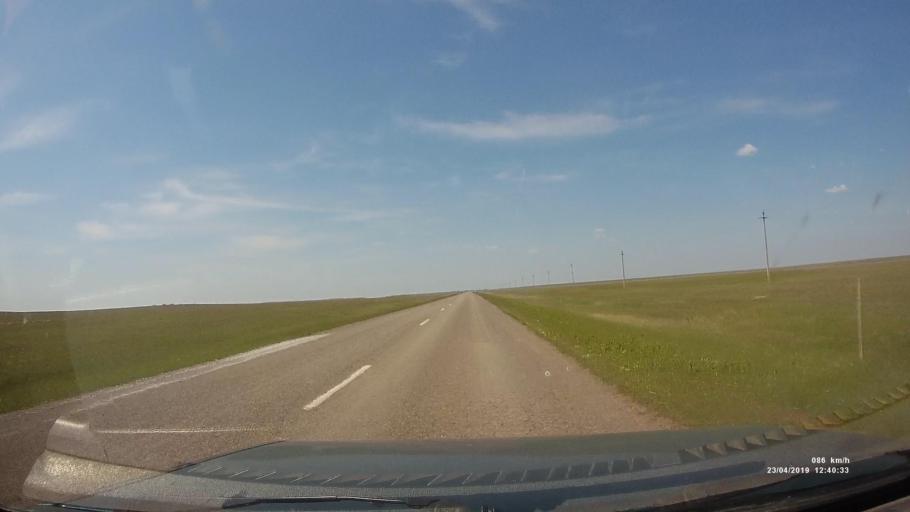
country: RU
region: Kalmykiya
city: Yashalta
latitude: 46.4412
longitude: 42.6948
